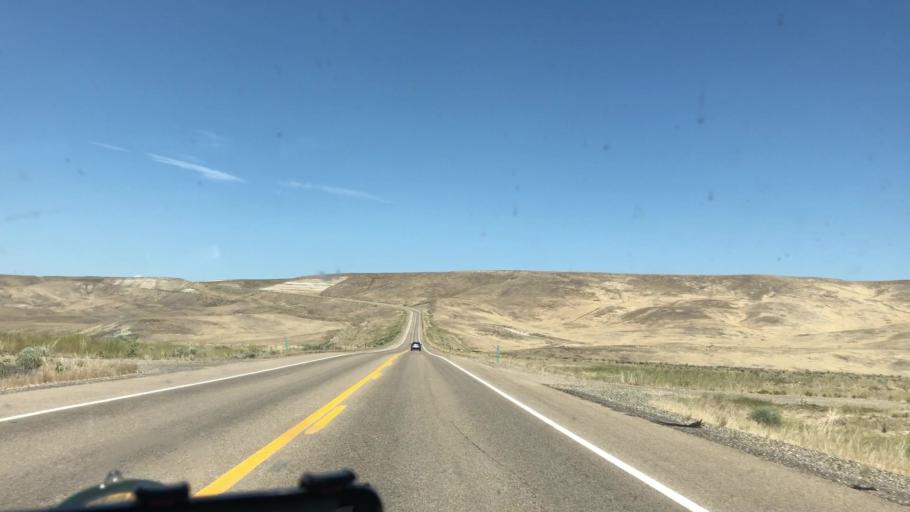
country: US
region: Idaho
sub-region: Owyhee County
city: Marsing
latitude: 43.2788
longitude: -116.9950
